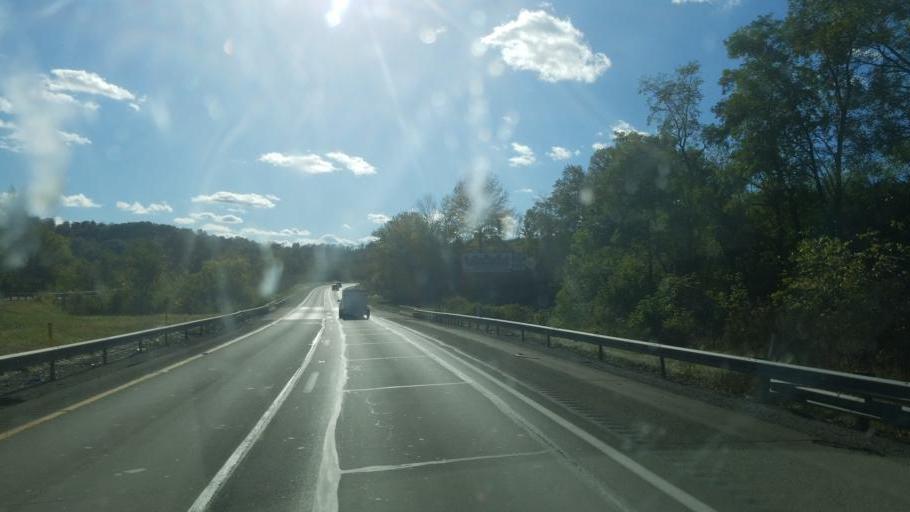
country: US
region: West Virginia
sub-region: Brooke County
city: Bethany
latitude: 40.1151
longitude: -80.4559
